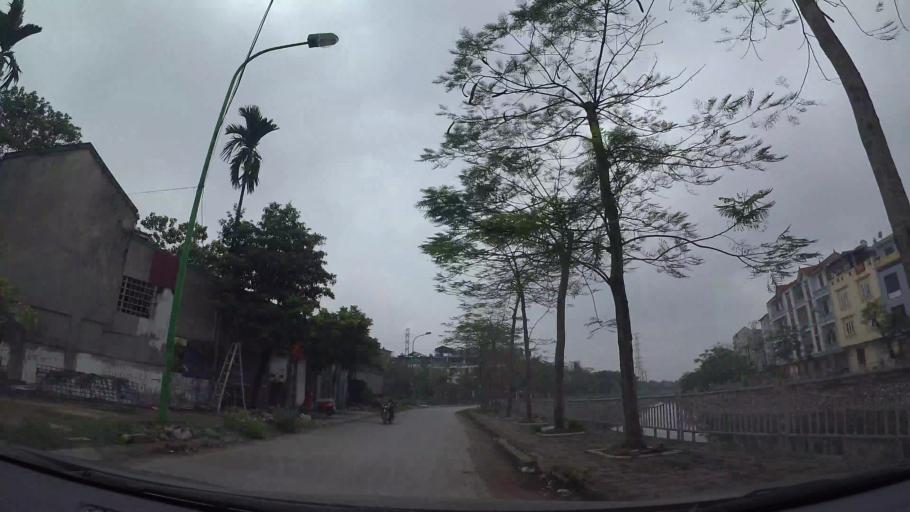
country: VN
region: Ha Noi
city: Van Dien
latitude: 20.9746
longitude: 105.8511
